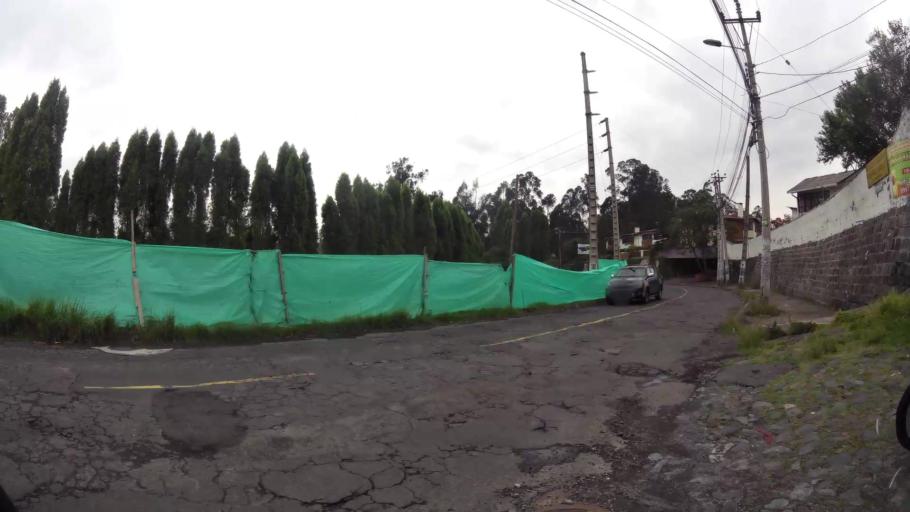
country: EC
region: Pichincha
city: Sangolqui
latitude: -0.3024
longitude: -78.4632
